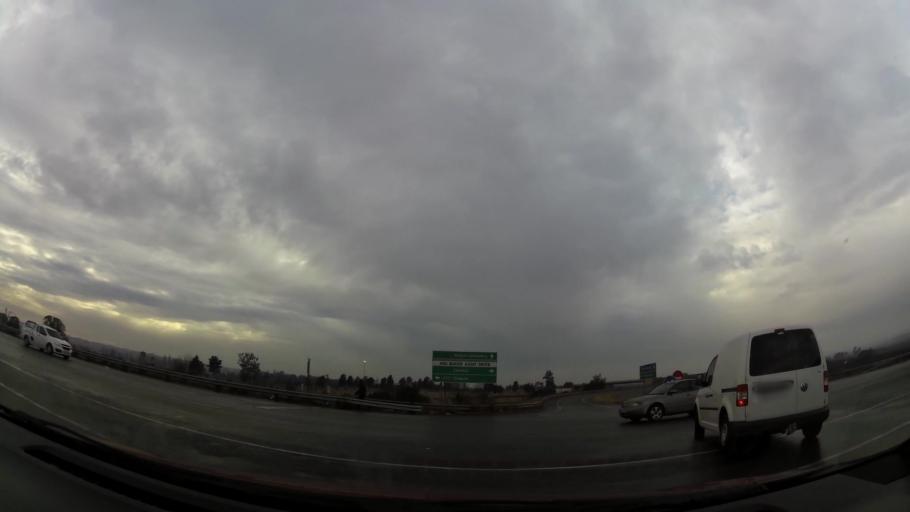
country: ZA
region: Gauteng
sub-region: City of Johannesburg Metropolitan Municipality
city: Soweto
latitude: -26.2990
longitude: 27.8480
